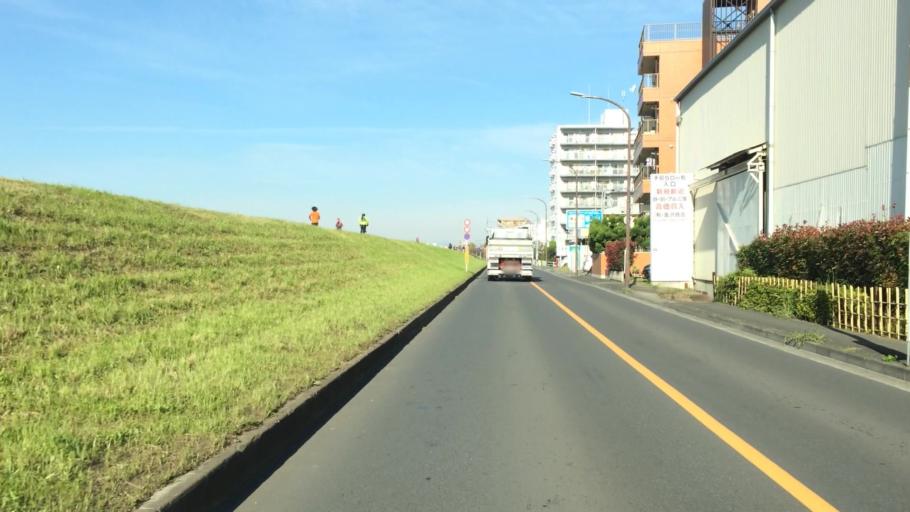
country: JP
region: Tokyo
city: Chofugaoka
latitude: 35.6473
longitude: 139.5243
